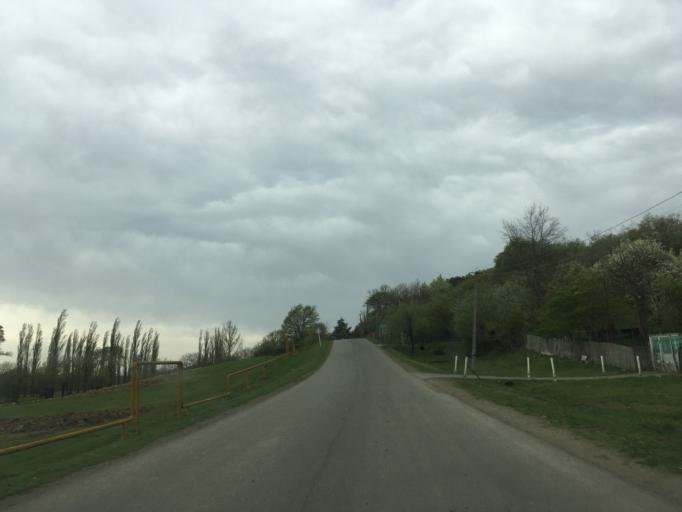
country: GE
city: Surami
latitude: 42.2228
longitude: 43.4431
